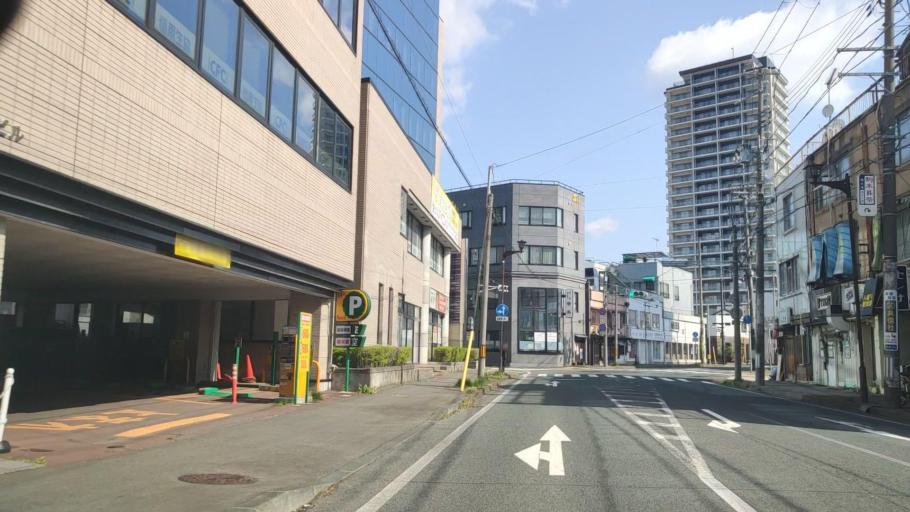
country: JP
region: Iwate
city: Morioka-shi
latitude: 39.6976
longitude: 141.1565
